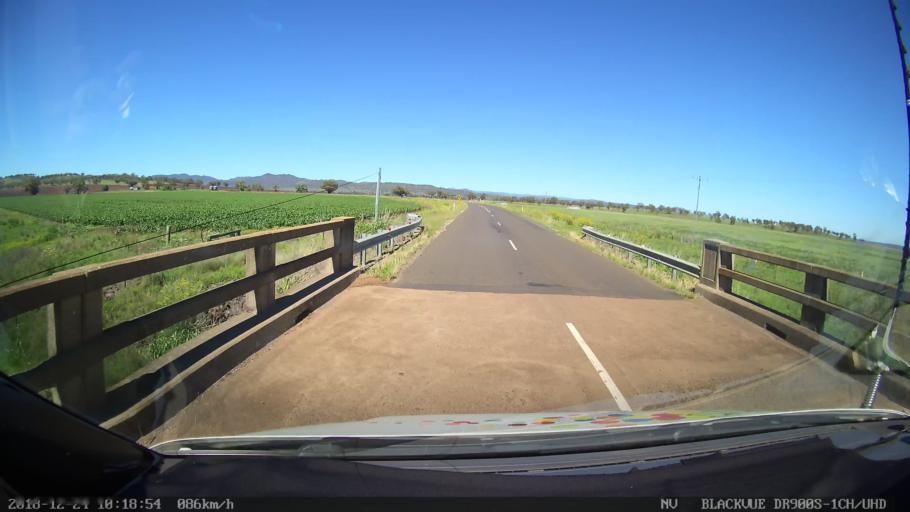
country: AU
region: New South Wales
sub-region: Liverpool Plains
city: Quirindi
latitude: -31.7256
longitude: 150.5696
